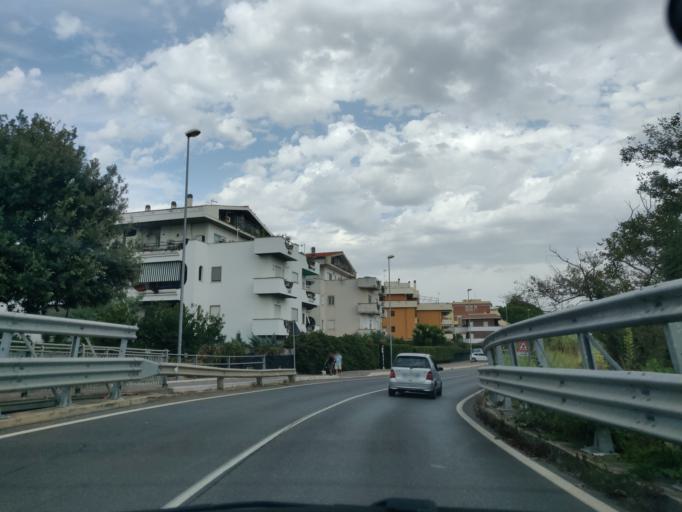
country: IT
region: Latium
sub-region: Citta metropolitana di Roma Capitale
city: Santa Marinella
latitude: 42.0404
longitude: 11.8829
